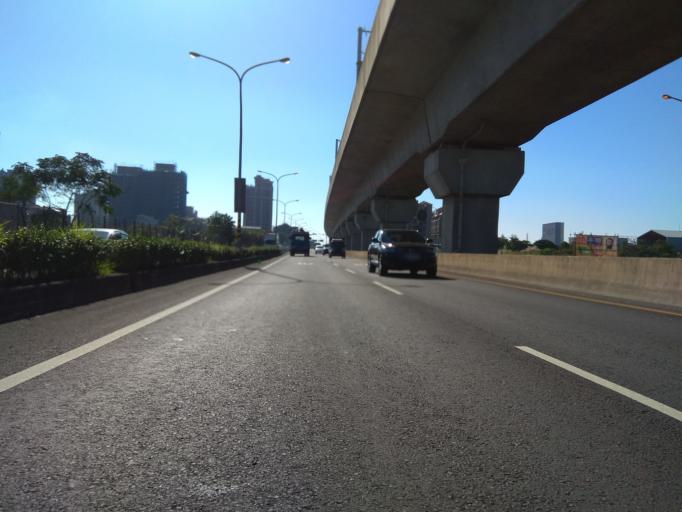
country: TW
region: Taiwan
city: Taoyuan City
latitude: 24.9650
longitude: 121.1668
